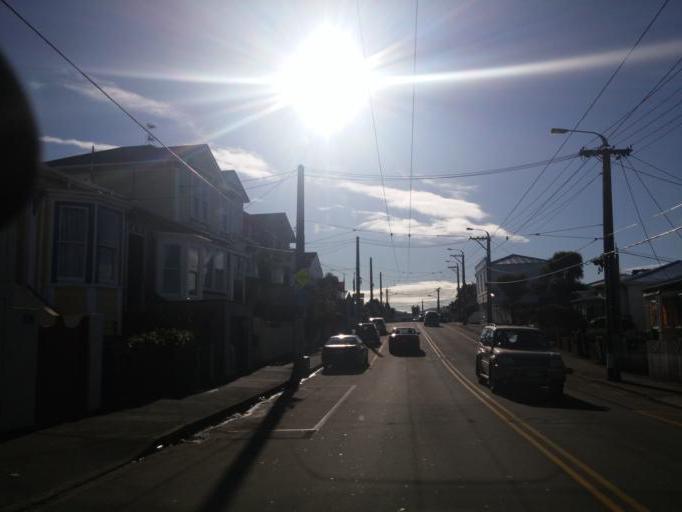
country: NZ
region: Wellington
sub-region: Wellington City
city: Wellington
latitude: -41.3058
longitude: 174.7750
